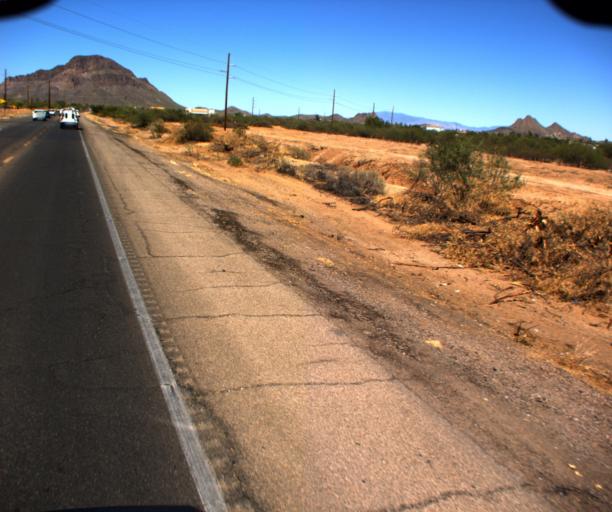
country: US
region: Arizona
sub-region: Pima County
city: Tucson Estates
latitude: 32.1616
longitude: -111.1012
